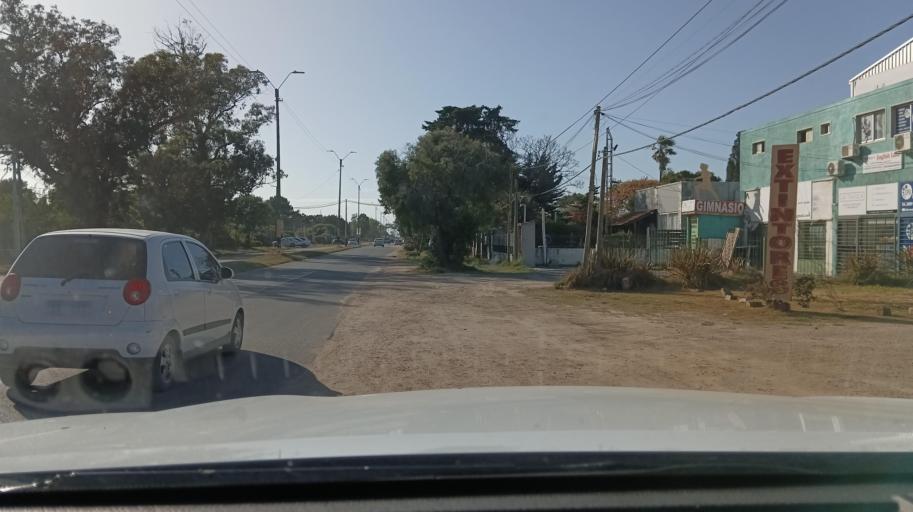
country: UY
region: Canelones
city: Barra de Carrasco
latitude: -34.8481
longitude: -56.0035
